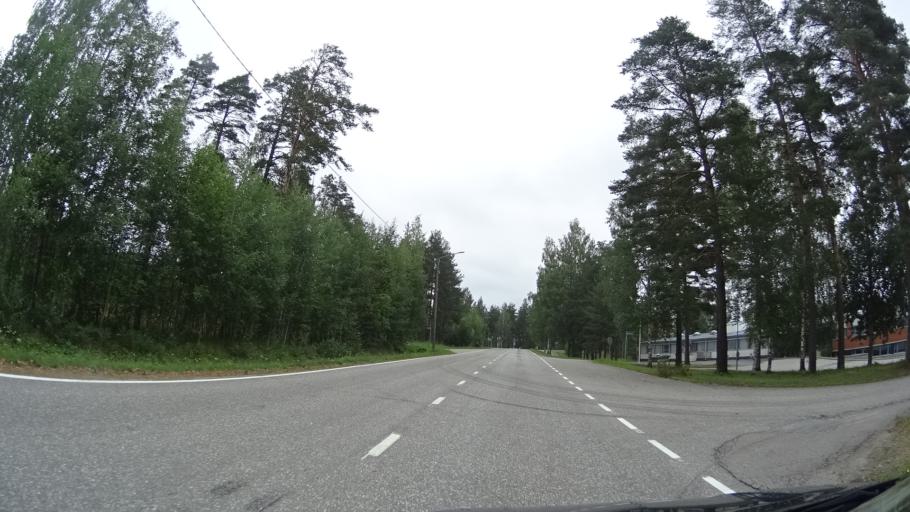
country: FI
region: Southern Savonia
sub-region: Savonlinna
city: Punkaharju
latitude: 61.7552
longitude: 29.3865
